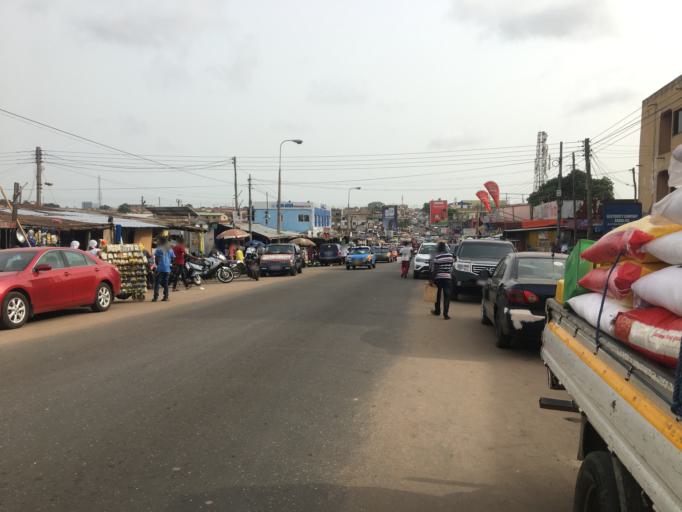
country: GH
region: Greater Accra
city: Accra
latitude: 5.5900
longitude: -0.1961
